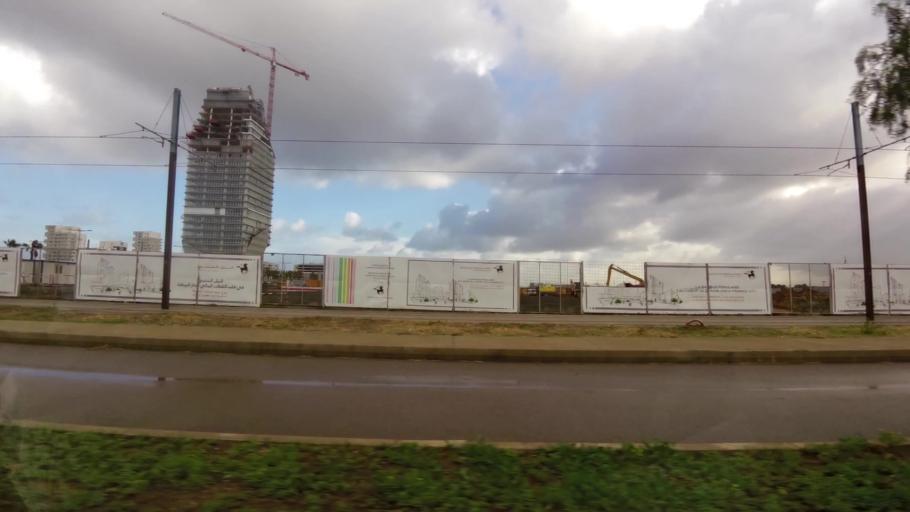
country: MA
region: Grand Casablanca
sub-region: Casablanca
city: Casablanca
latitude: 33.5614
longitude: -7.6613
